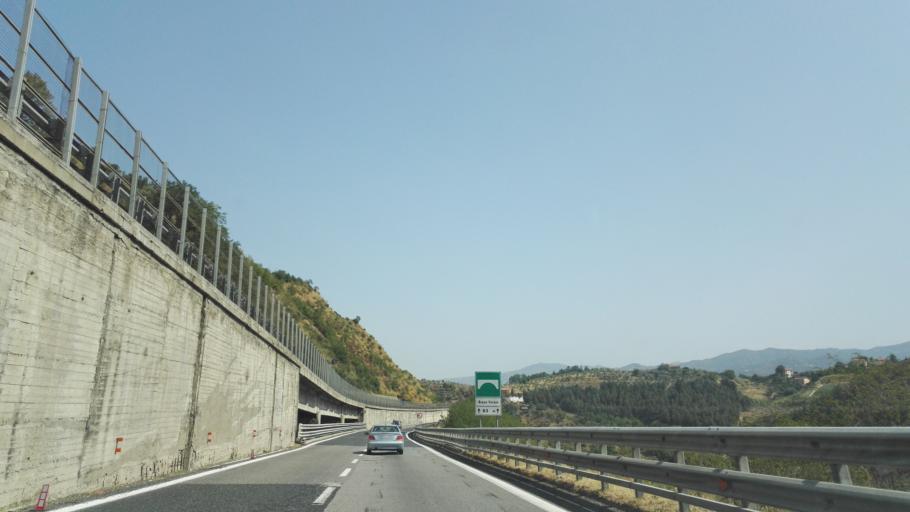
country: IT
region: Calabria
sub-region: Provincia di Cosenza
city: Laurignano
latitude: 39.2737
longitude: 16.2475
